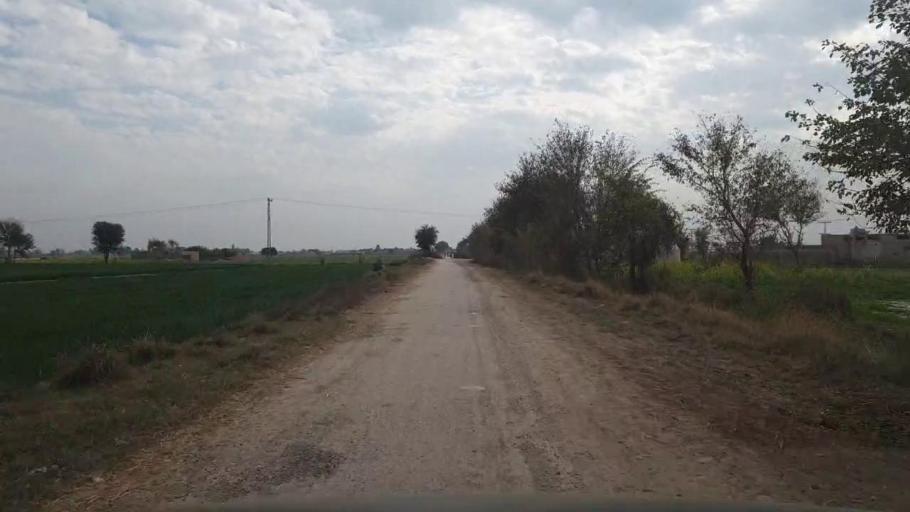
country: PK
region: Sindh
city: Sakrand
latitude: 26.0149
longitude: 68.4312
